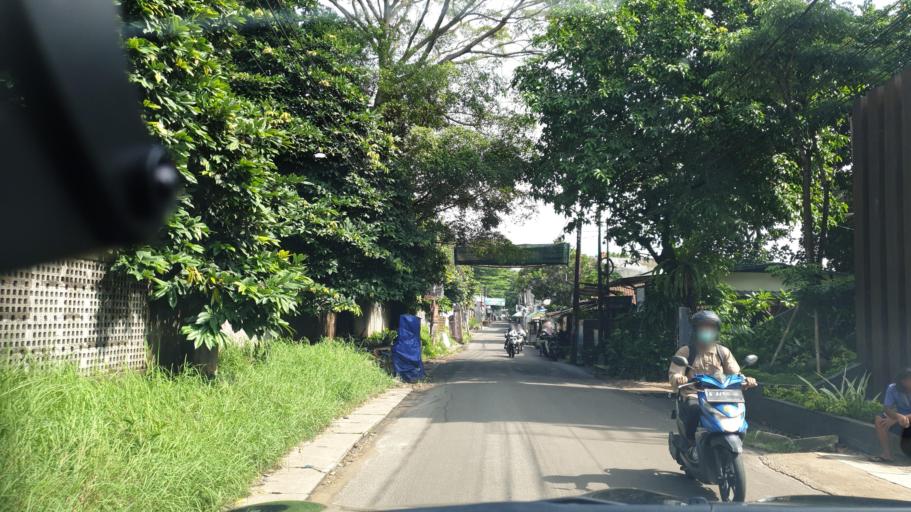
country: ID
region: West Java
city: Pamulang
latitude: -6.3072
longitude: 106.7659
